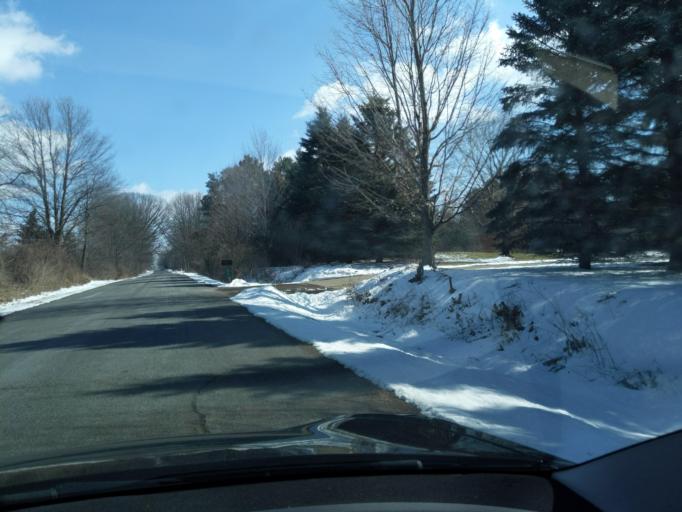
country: US
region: Michigan
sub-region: Ingham County
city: Mason
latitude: 42.6111
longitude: -84.4543
